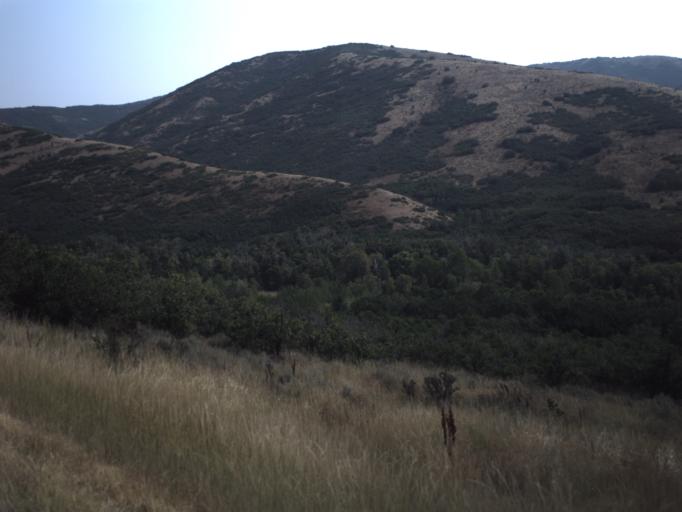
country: US
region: Utah
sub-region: Summit County
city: Summit Park
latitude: 40.7811
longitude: -111.6852
